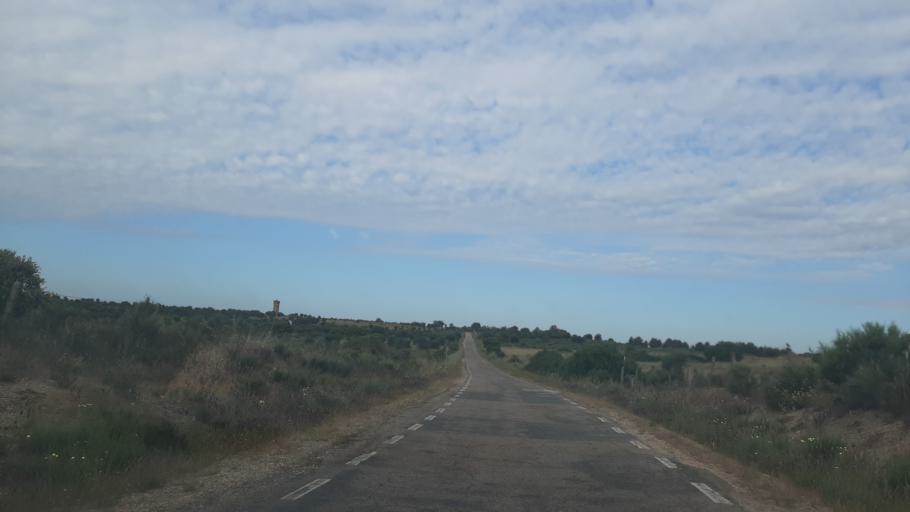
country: ES
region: Castille and Leon
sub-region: Provincia de Salamanca
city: Fuentes de Onoro
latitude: 40.6426
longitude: -6.7953
